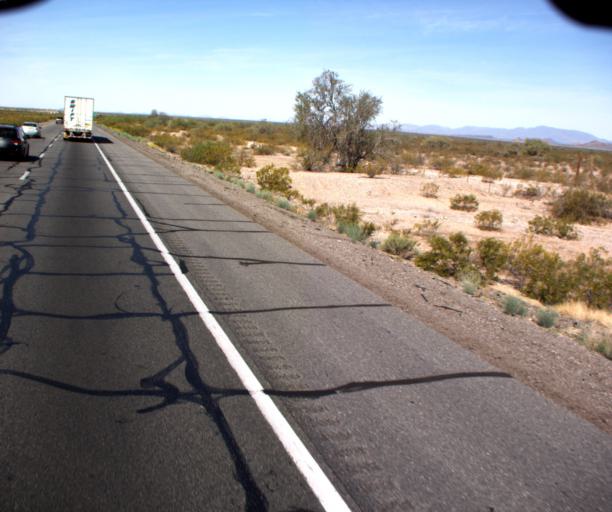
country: US
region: Arizona
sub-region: La Paz County
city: Salome
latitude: 33.5316
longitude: -113.1271
